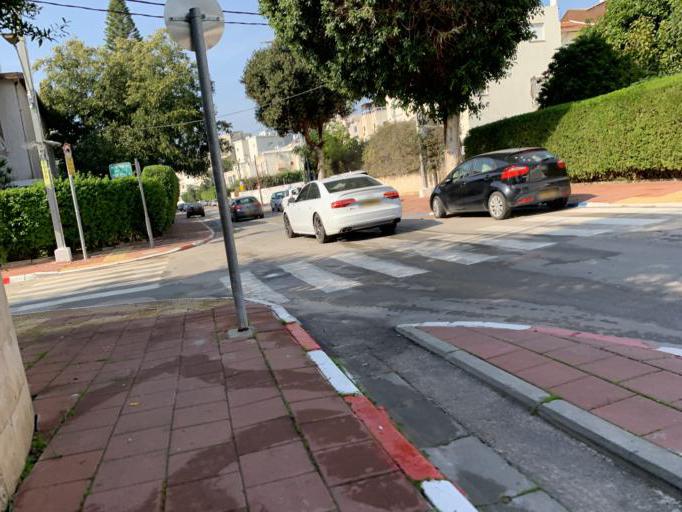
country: IL
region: Tel Aviv
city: Ramat Gan
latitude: 32.0943
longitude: 34.8117
